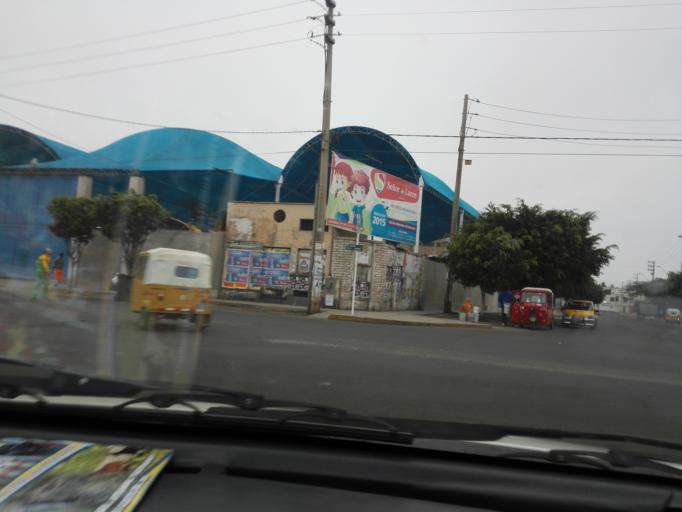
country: PE
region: Ica
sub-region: Provincia de Ica
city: Ica
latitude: -14.0716
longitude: -75.7271
